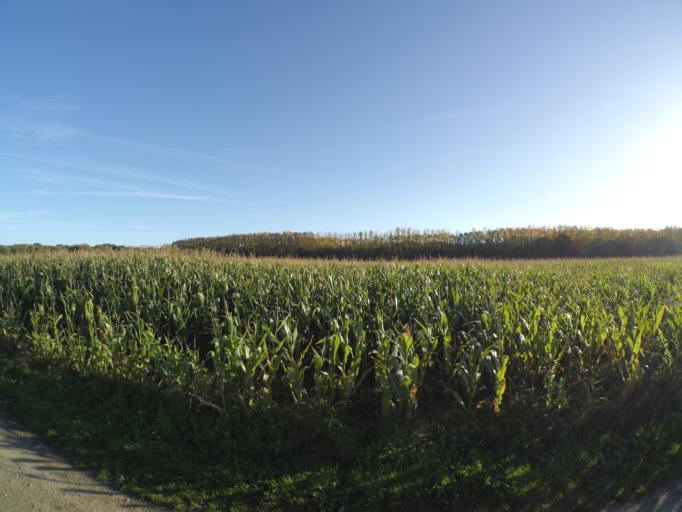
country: FR
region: Brittany
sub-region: Departement du Morbihan
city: Saint-Vincent-sur-Oust
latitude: 47.7238
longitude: -2.1735
